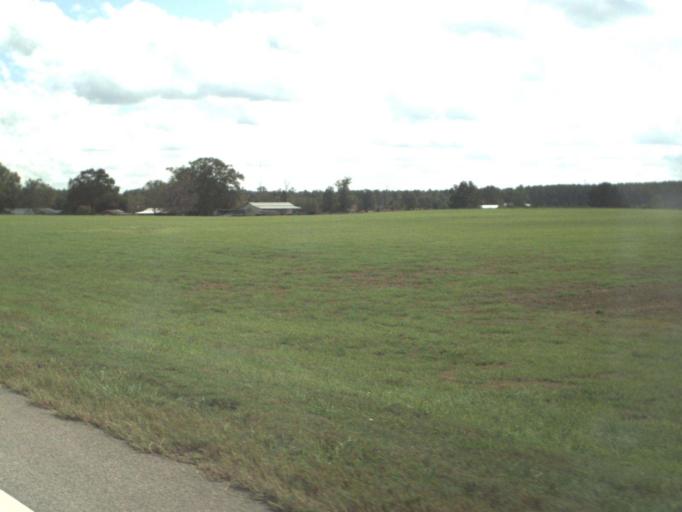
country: US
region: Florida
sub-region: Jackson County
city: Marianna
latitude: 30.8133
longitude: -85.3042
